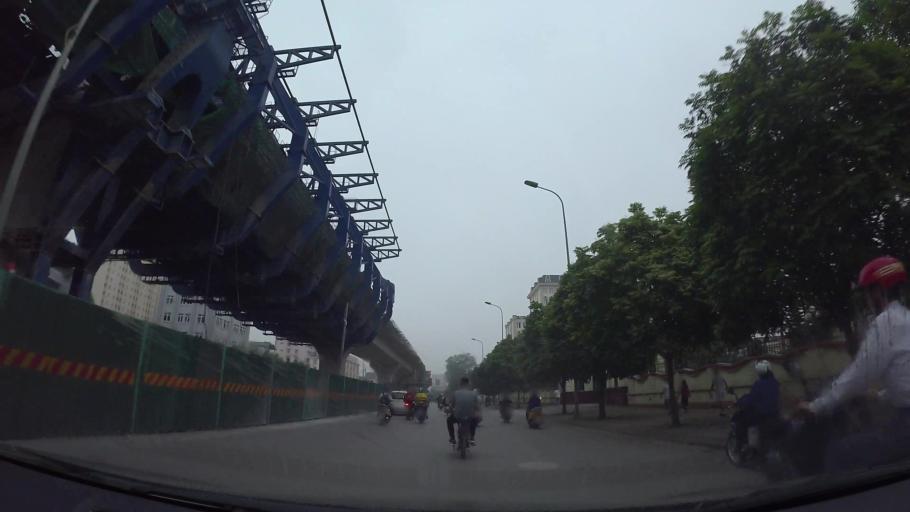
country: VN
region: Ha Noi
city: Dong Da
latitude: 20.9996
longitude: 105.8323
